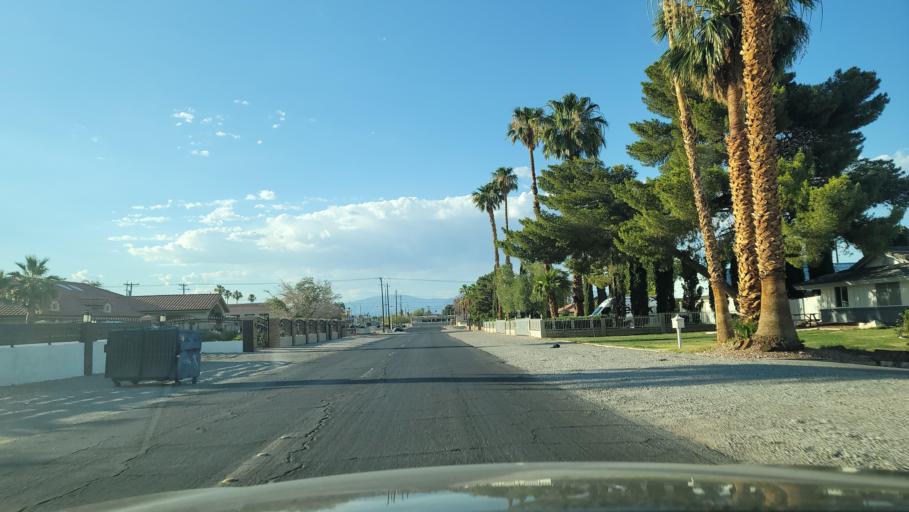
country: US
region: Nevada
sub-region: Clark County
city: Spring Valley
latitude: 36.1561
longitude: -115.2191
